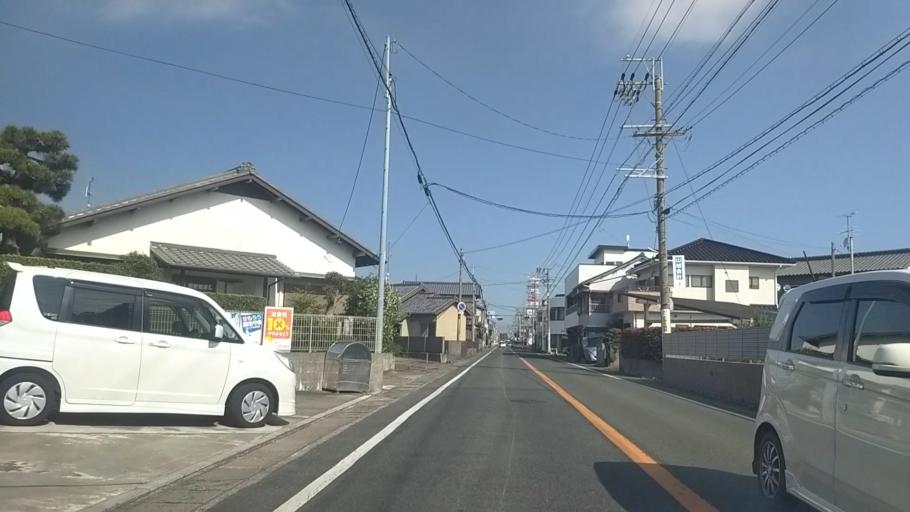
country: JP
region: Shizuoka
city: Hamamatsu
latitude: 34.7007
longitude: 137.7568
